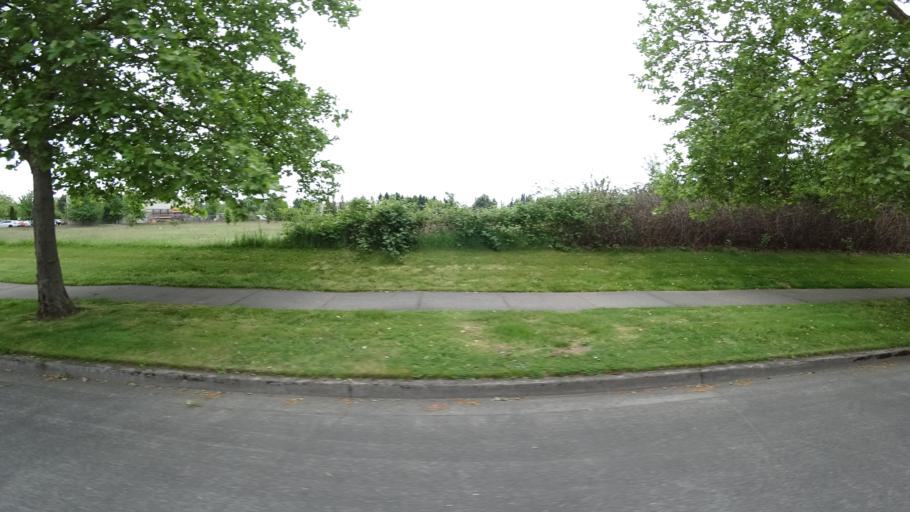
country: US
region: Oregon
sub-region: Washington County
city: Aloha
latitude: 45.4977
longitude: -122.9251
